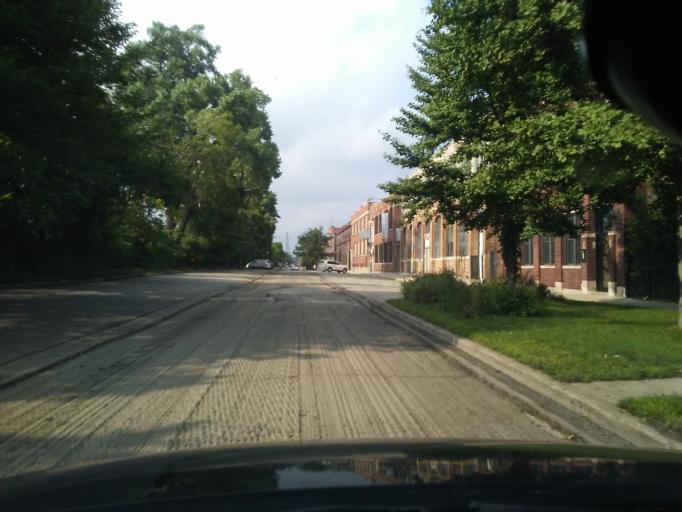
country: US
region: Illinois
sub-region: Cook County
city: Lincolnwood
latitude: 41.9599
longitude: -87.6739
